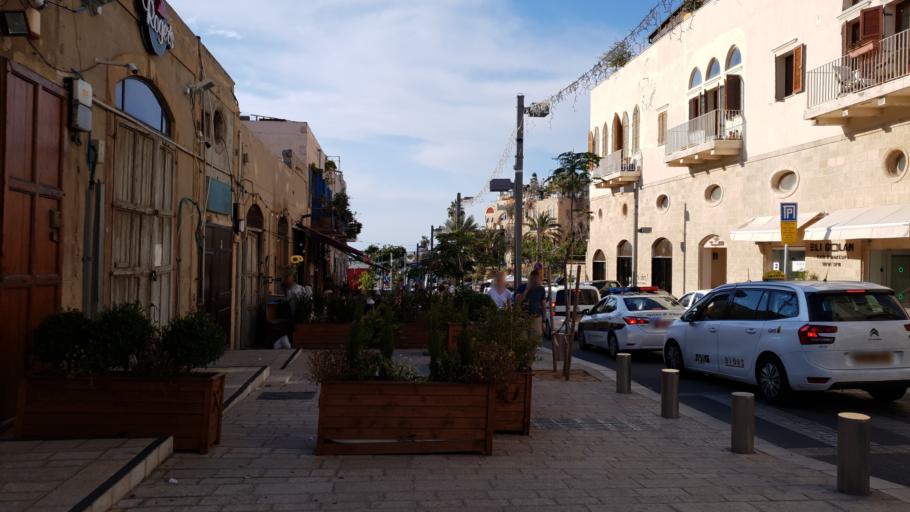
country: IL
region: Tel Aviv
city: Yafo
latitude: 32.0525
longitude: 34.7524
